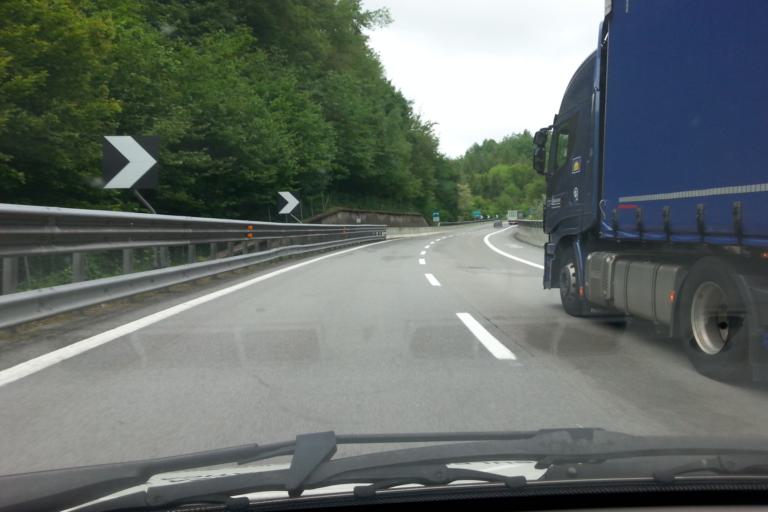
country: IT
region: Piedmont
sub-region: Provincia di Cuneo
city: Castelnuovo di Ceva
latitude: 44.3575
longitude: 8.1497
